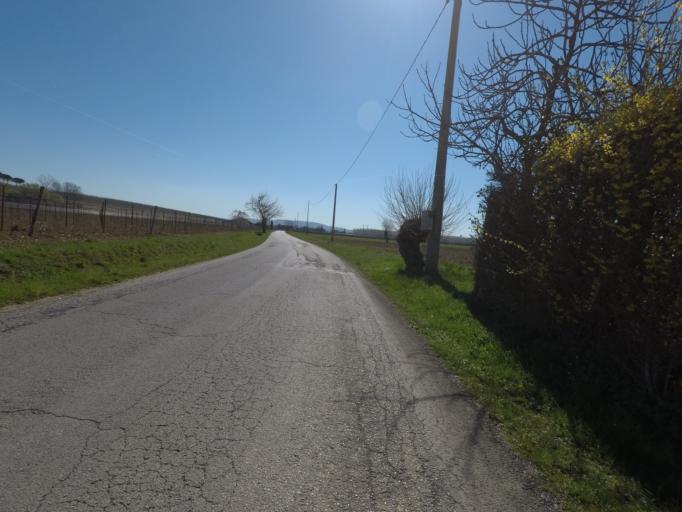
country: IT
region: Friuli Venezia Giulia
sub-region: Provincia di Gorizia
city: Cormons
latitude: 45.9401
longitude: 13.4734
